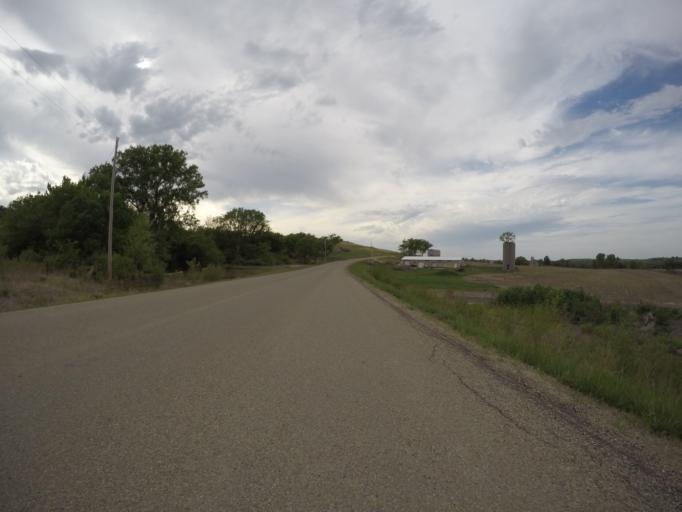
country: US
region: Kansas
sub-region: Riley County
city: Ogden
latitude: 39.0473
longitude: -96.6398
